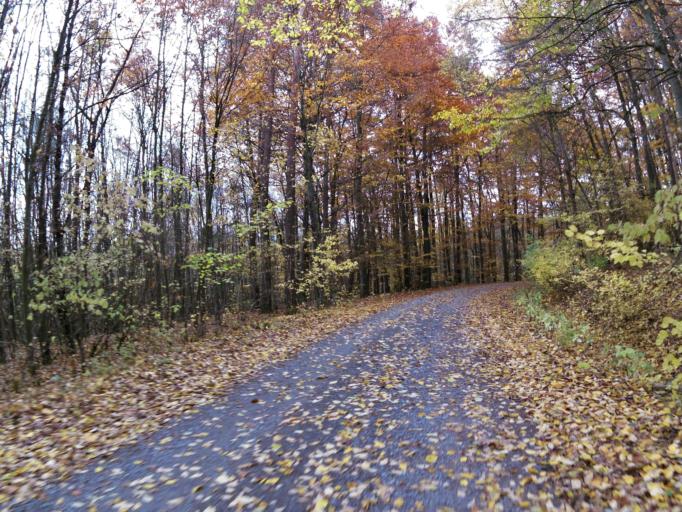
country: DE
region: Bavaria
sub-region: Regierungsbezirk Unterfranken
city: Eisingen
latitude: 49.7468
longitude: 9.8215
